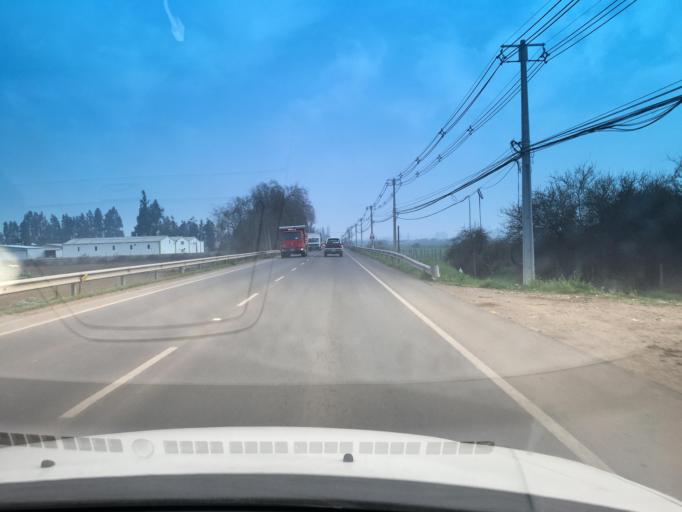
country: CL
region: Santiago Metropolitan
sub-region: Provincia de Chacabuco
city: Lampa
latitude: -33.3388
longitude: -70.8148
